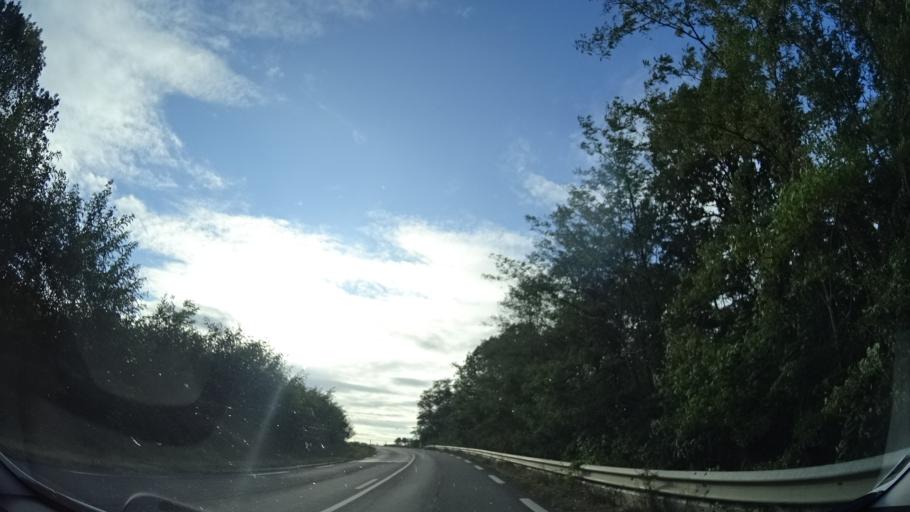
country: FR
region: Centre
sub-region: Departement du Loir-et-Cher
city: Moree
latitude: 47.8946
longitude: 1.1674
